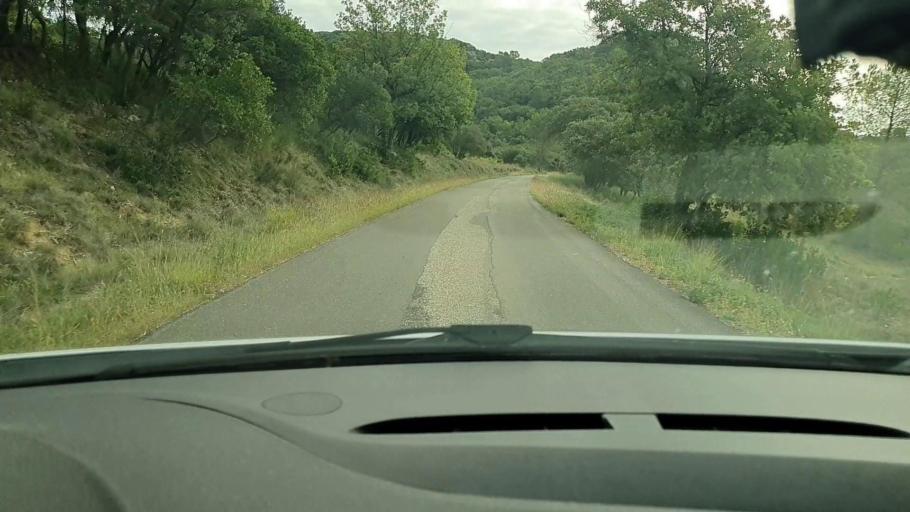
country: FR
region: Languedoc-Roussillon
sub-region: Departement du Gard
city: Montaren-et-Saint-Mediers
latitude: 44.0942
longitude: 4.3241
